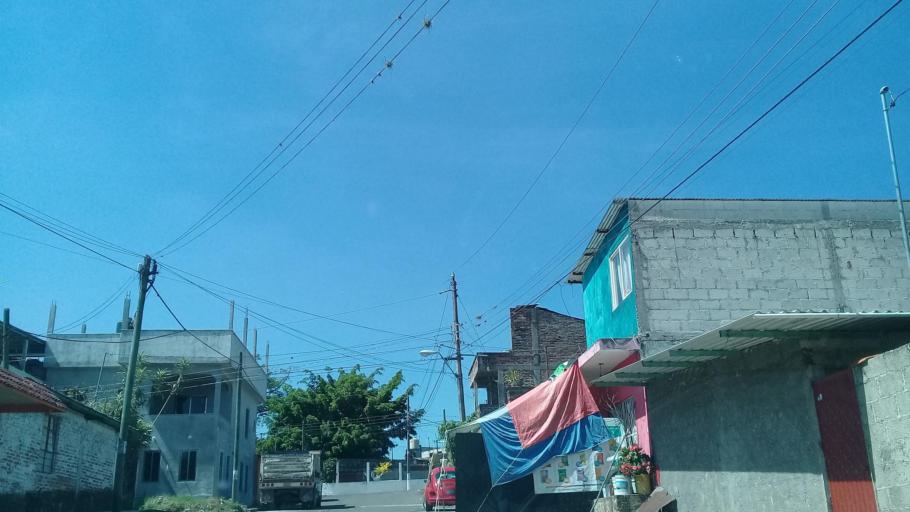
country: MX
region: Veracruz
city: Amatlan de los Reyes
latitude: 18.8423
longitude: -96.9124
